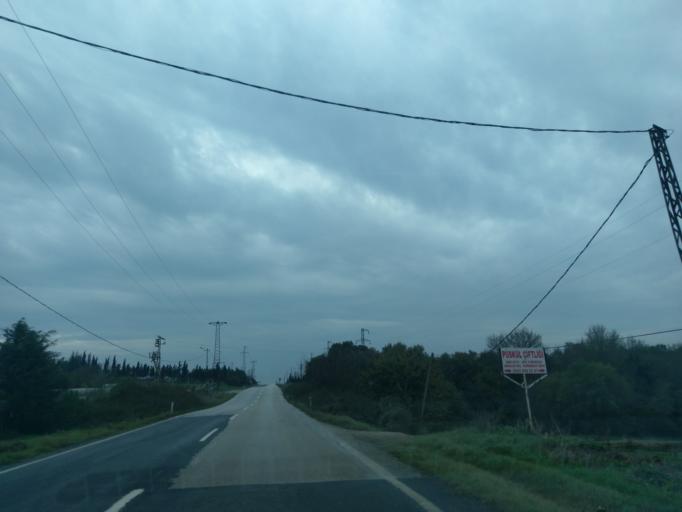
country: TR
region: Istanbul
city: Canta
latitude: 41.1403
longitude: 28.1069
